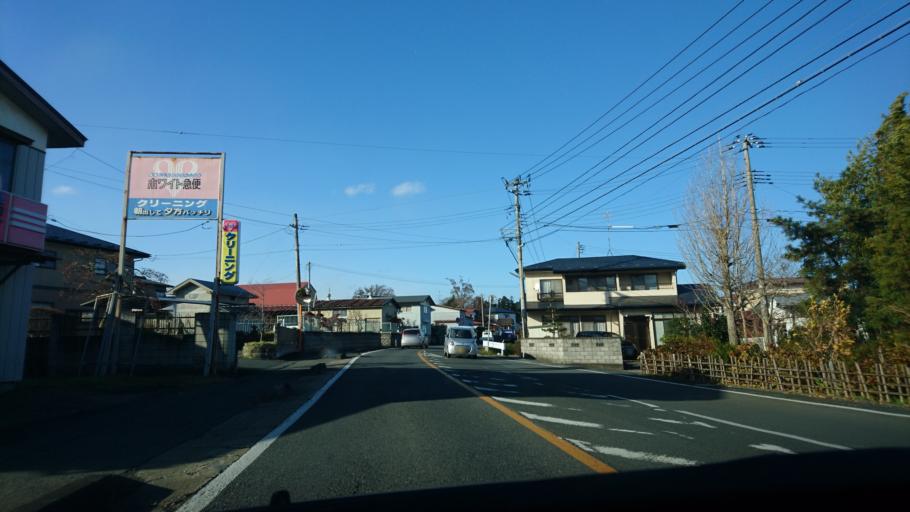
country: JP
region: Iwate
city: Mizusawa
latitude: 39.1181
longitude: 141.1655
